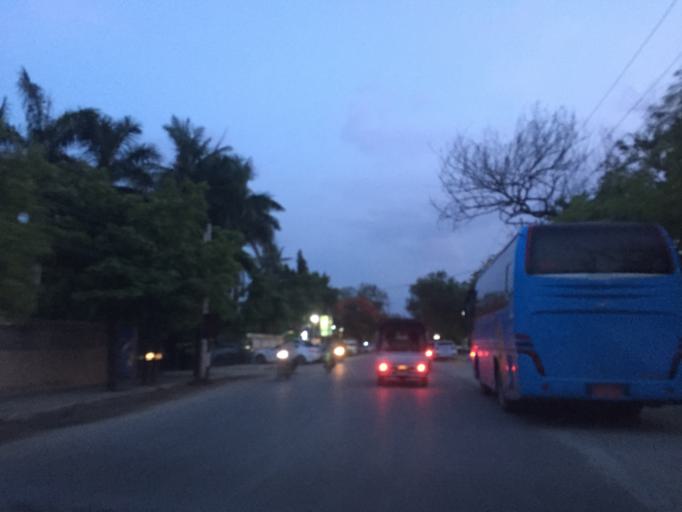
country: MM
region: Mandalay
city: Mandalay
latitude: 21.9792
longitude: 96.1198
